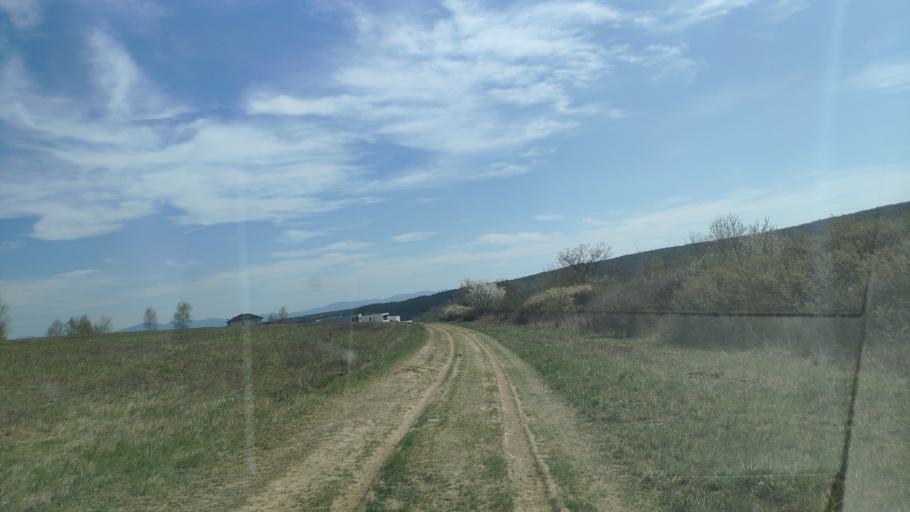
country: SK
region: Kosicky
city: Kosice
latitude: 48.7202
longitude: 21.1980
